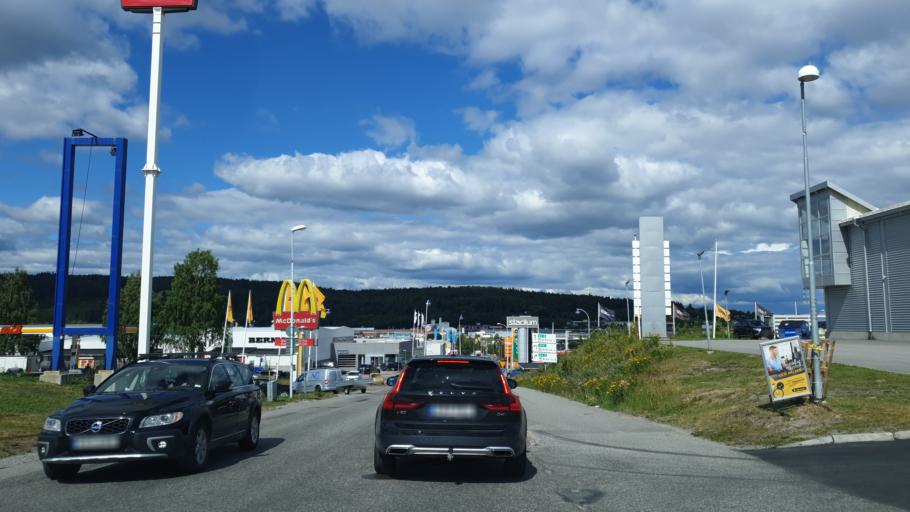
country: SE
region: Vaesternorrland
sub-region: Sundsvalls Kommun
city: Sundsbruk
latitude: 62.4409
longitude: 17.3315
